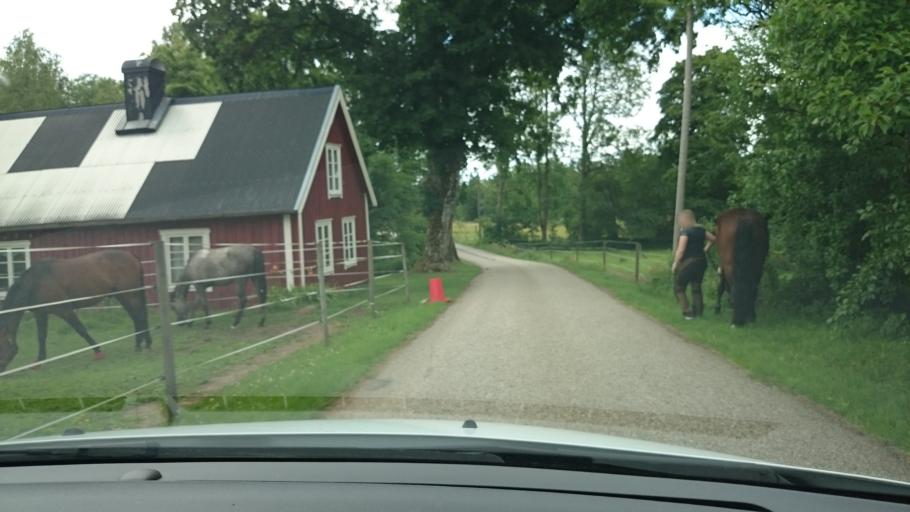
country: SE
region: Halland
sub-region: Hylte Kommun
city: Hyltebruk
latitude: 56.9668
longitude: 13.1973
